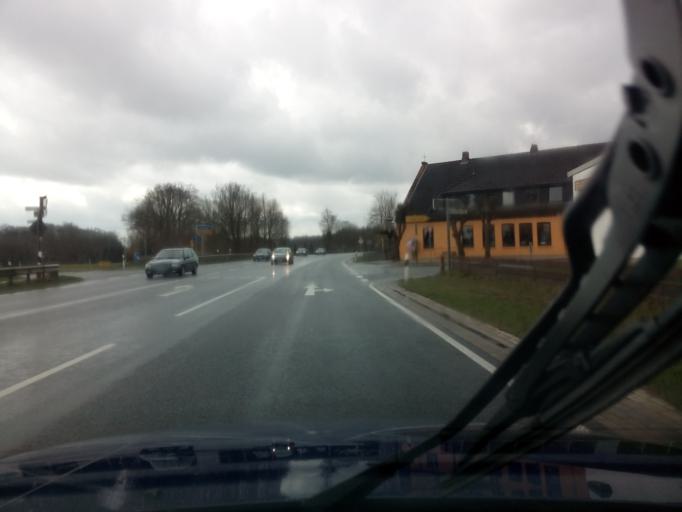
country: DE
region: Lower Saxony
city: Prinzhofte
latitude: 52.9792
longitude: 8.5297
